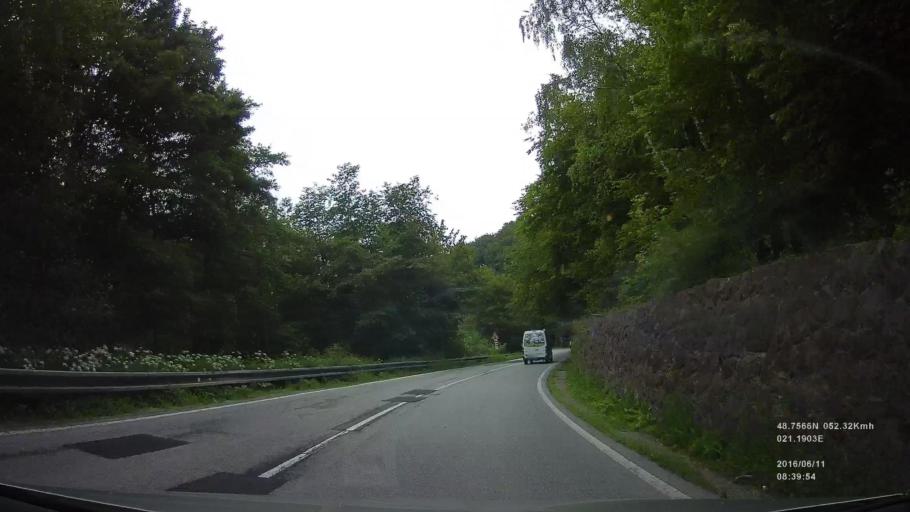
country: SK
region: Kosicky
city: Kosice
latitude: 48.7539
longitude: 21.1980
